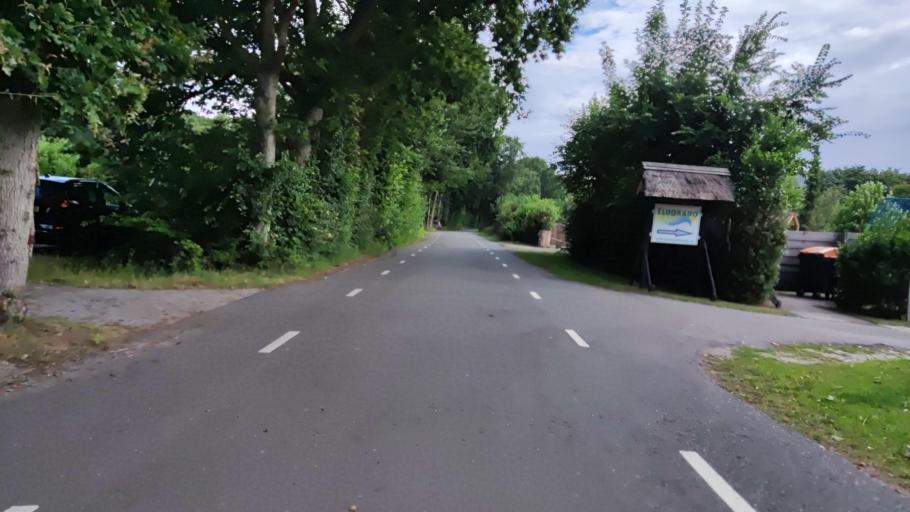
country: NL
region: North Holland
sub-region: Gemeente Texel
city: Den Burg
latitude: 53.0822
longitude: 4.7646
